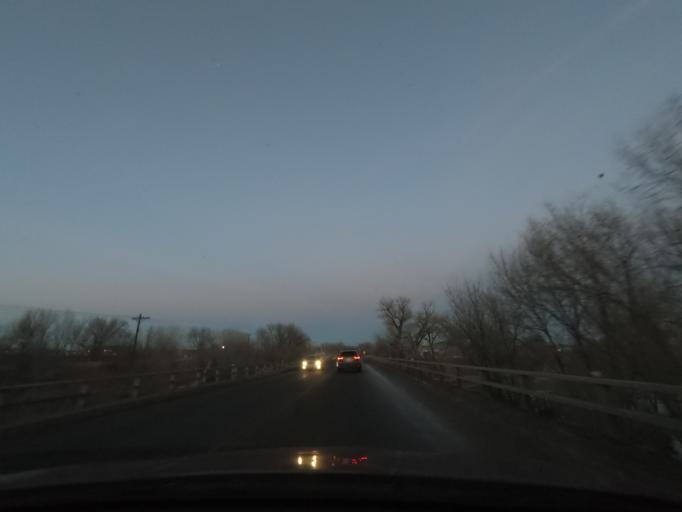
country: US
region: Colorado
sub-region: El Paso County
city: Stratmoor
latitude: 38.7764
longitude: -104.7796
